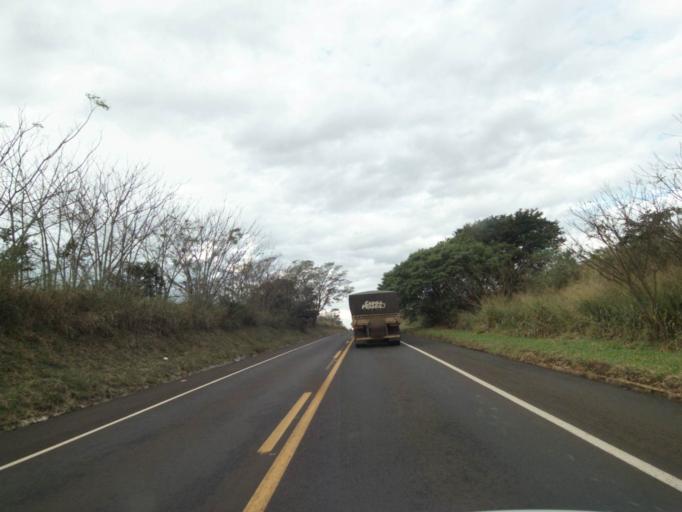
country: PY
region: Canindeyu
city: Salto del Guaira
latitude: -24.0831
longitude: -54.0896
